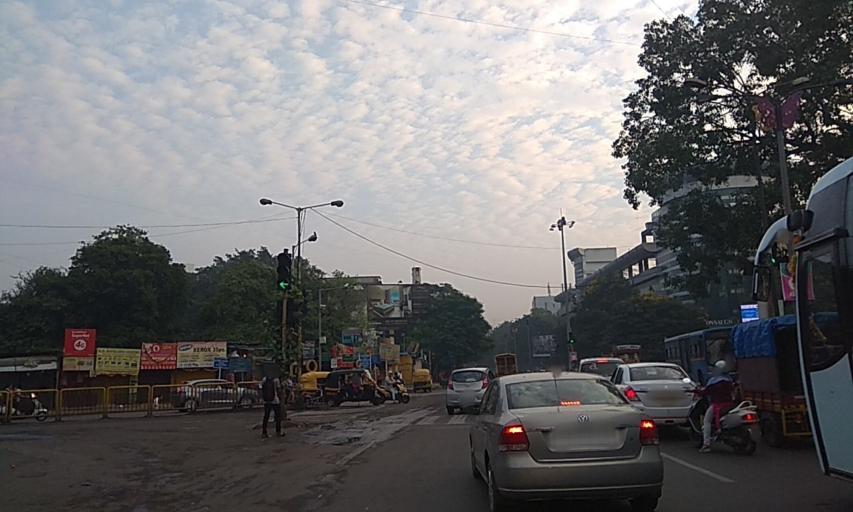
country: IN
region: Maharashtra
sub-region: Pune Division
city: Shivaji Nagar
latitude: 18.5344
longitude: 73.8793
